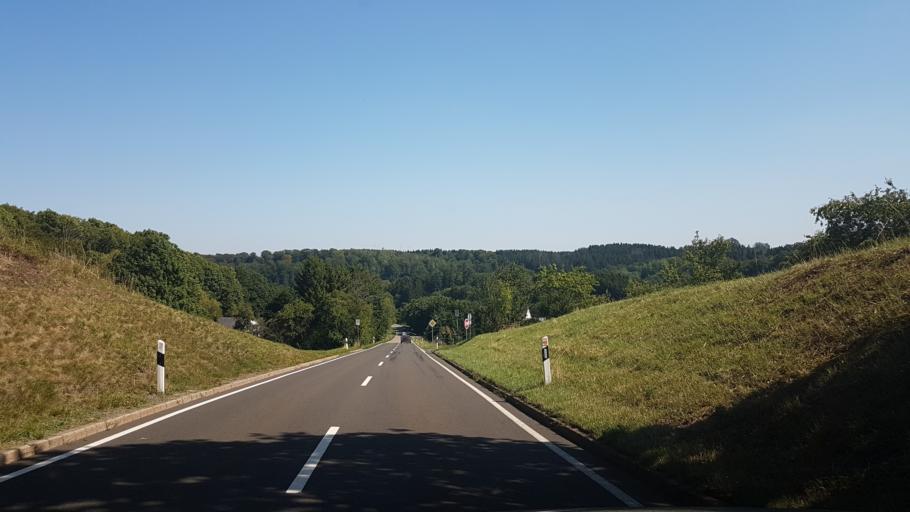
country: DE
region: Rheinland-Pfalz
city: Rohrbach
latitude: 49.5857
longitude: 7.2591
